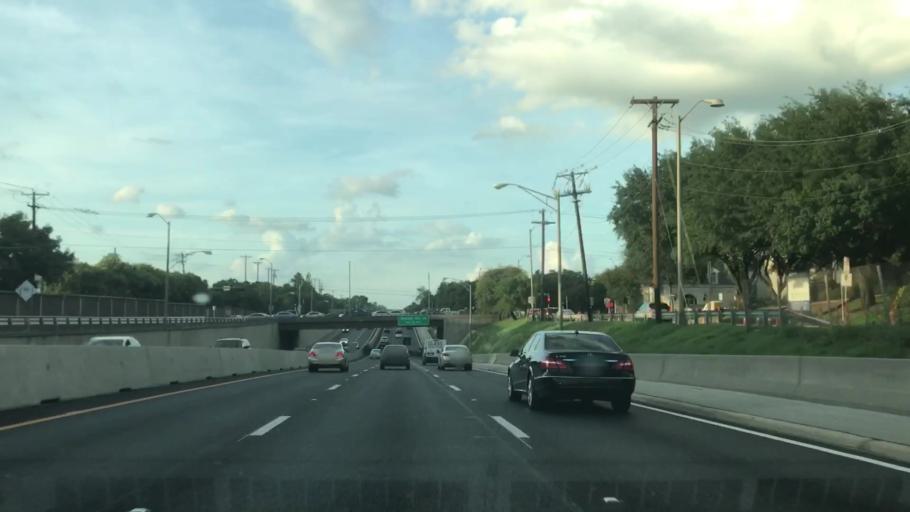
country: US
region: Texas
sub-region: Dallas County
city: University Park
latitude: 32.8642
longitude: -96.8116
